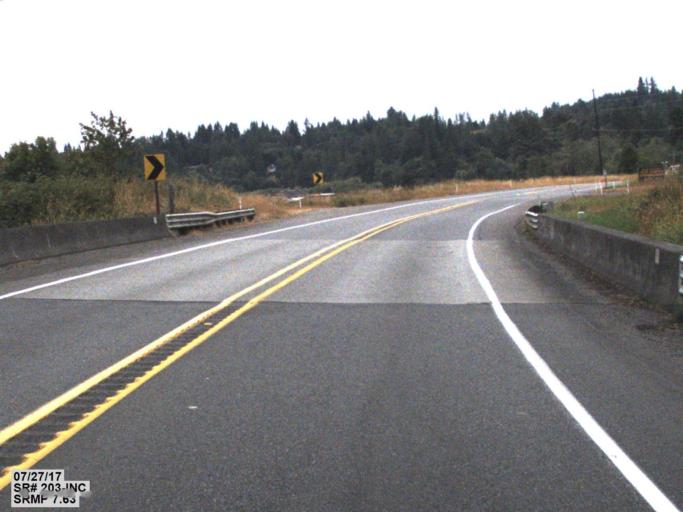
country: US
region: Washington
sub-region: King County
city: Lake Marcel-Stillwater
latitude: 47.6715
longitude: -121.9083
